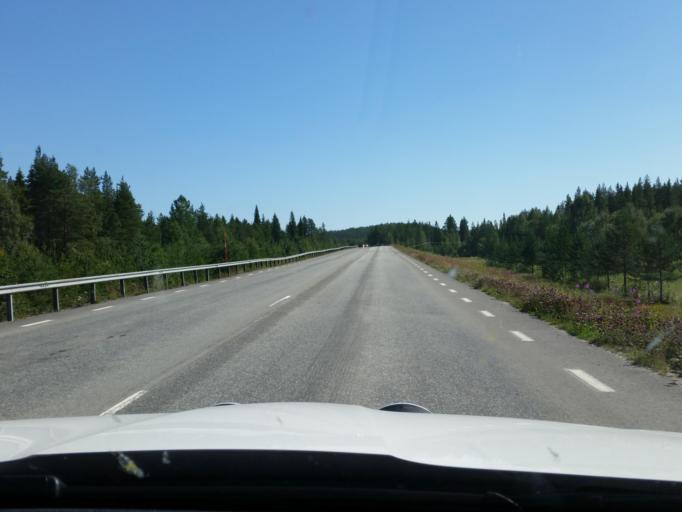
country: SE
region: Norrbotten
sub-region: Alvsbyns Kommun
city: AElvsbyn
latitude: 65.6699
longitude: 20.9585
